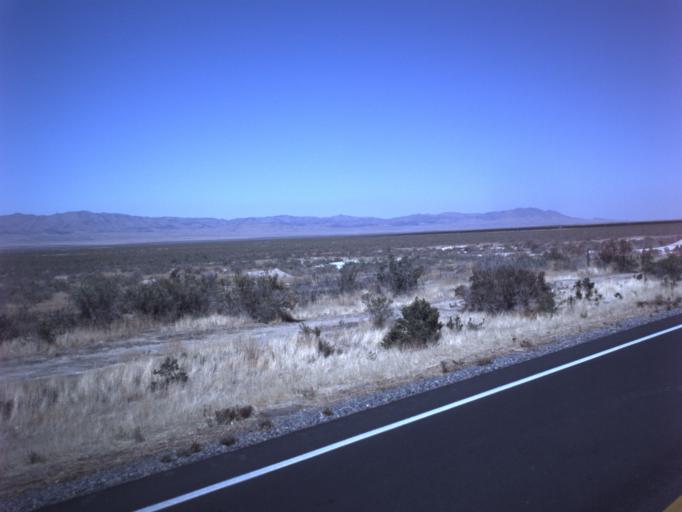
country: US
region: Utah
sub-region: Tooele County
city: Grantsville
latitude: 40.4734
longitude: -112.7462
